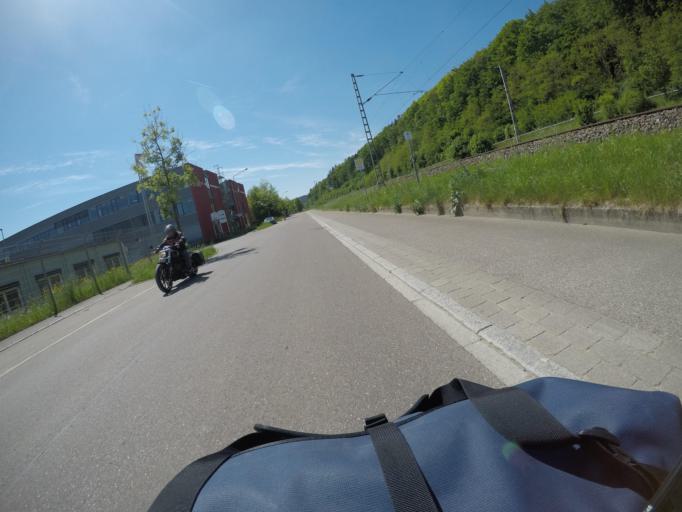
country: DE
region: Baden-Wuerttemberg
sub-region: Regierungsbezirk Stuttgart
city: Schwabisch Gmund
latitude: 48.7889
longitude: 9.7576
